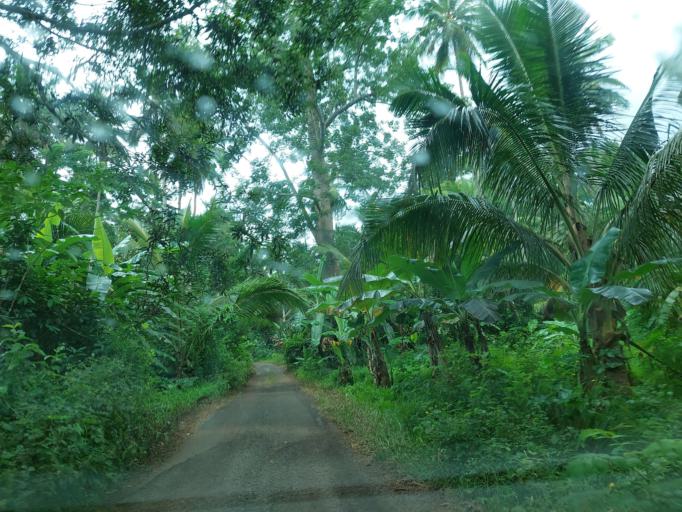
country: YT
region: Tsingoni
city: Tsingoni
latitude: -12.7675
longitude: 45.1153
